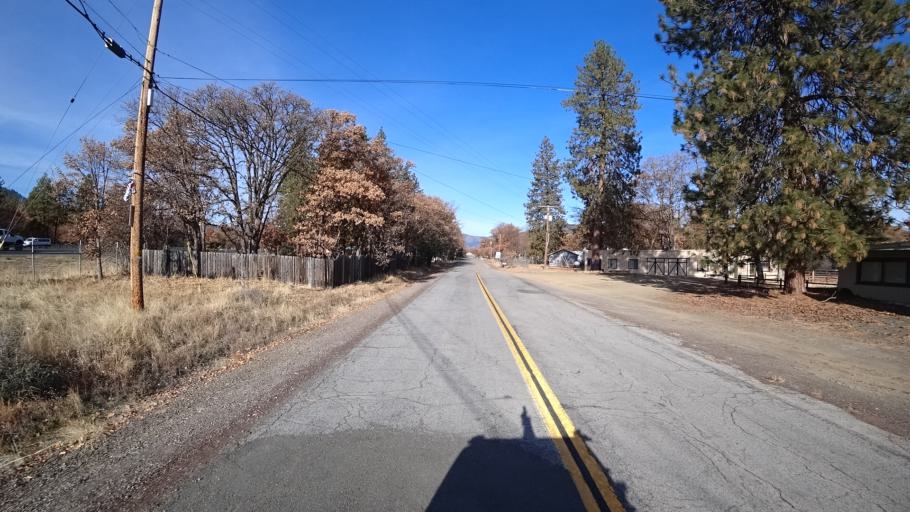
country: US
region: California
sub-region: Siskiyou County
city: Yreka
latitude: 41.6638
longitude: -122.6020
